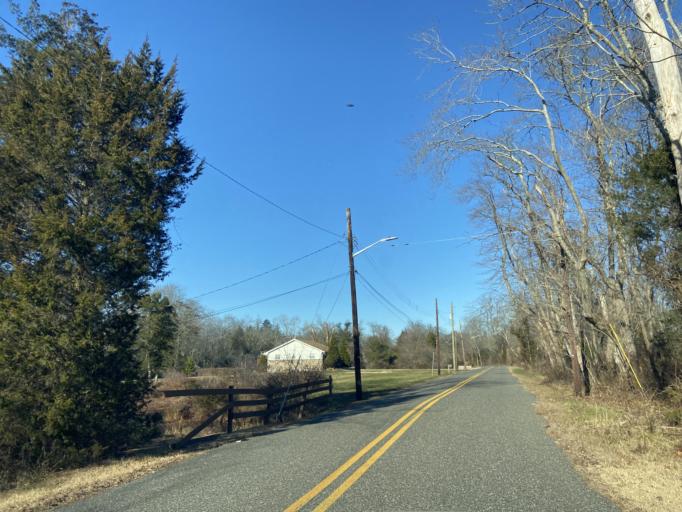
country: US
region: New Jersey
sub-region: Cumberland County
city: Vineland
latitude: 39.4925
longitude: -75.0736
